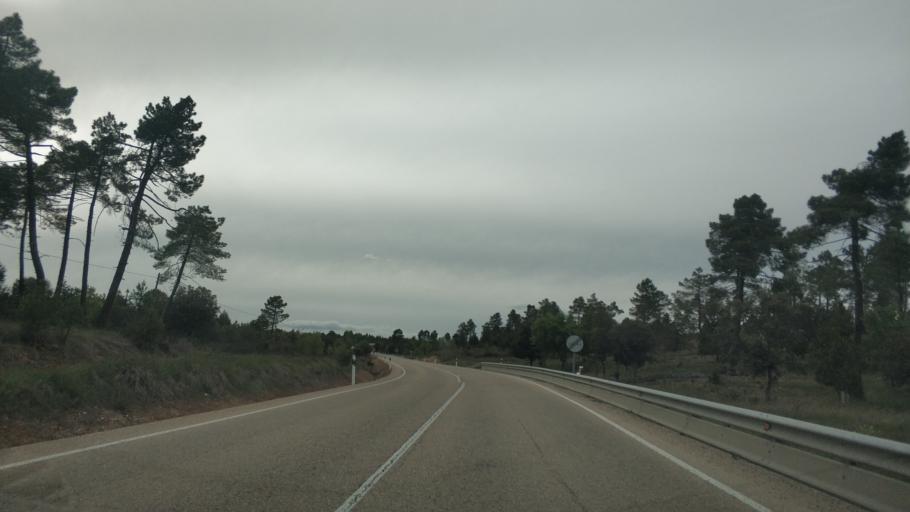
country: ES
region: Castille and Leon
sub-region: Provincia de Soria
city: Bayubas de Abajo
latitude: 41.5215
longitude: -2.9349
